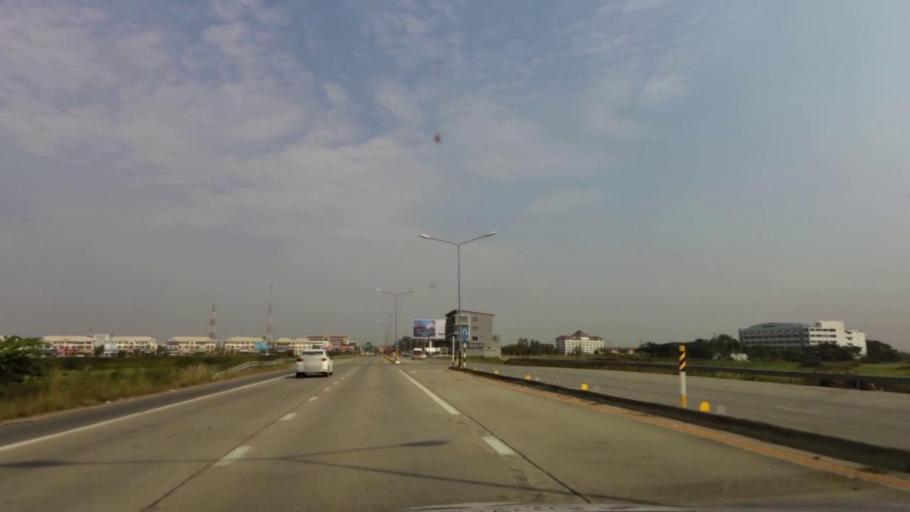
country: TH
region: Phra Nakhon Si Ayutthaya
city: Phra Nakhon Si Ayutthaya
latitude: 14.3332
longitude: 100.6019
